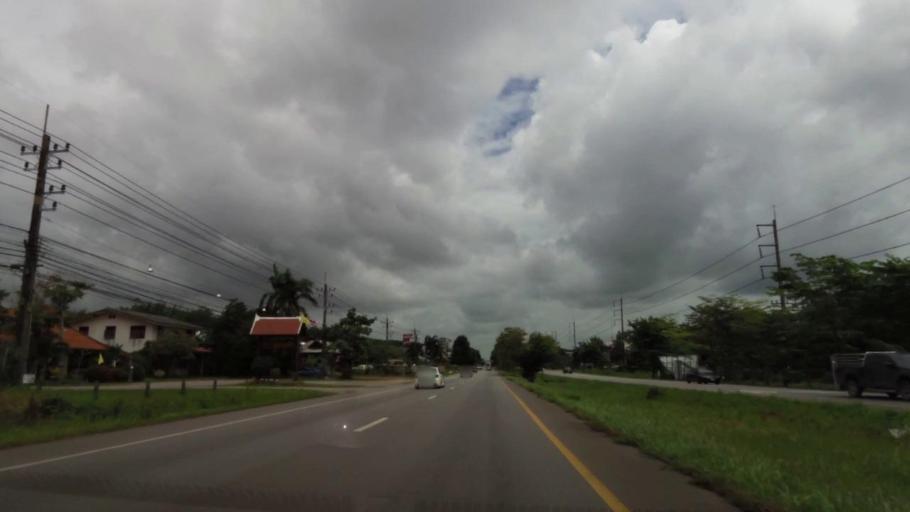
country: TH
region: Chanthaburi
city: Na Yai Am
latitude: 12.7676
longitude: 101.8490
